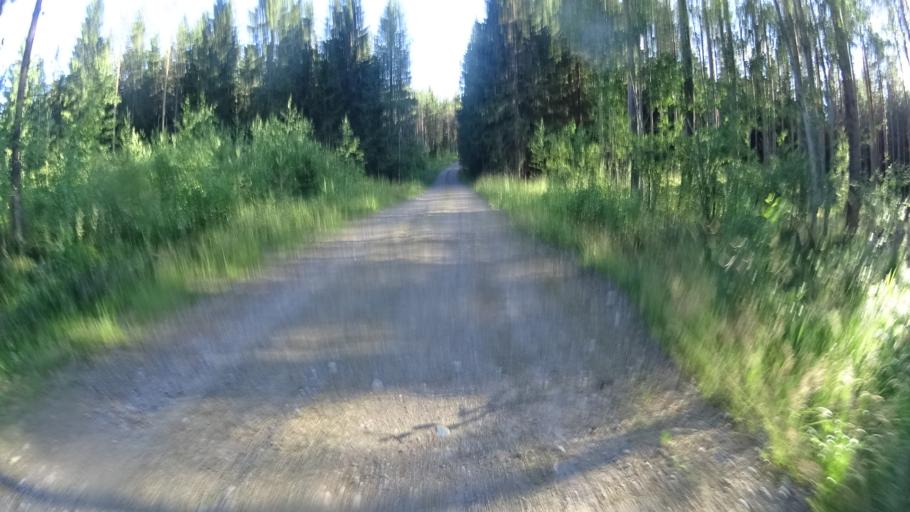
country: FI
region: Uusimaa
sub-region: Helsinki
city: Karkkila
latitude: 60.6533
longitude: 24.1309
